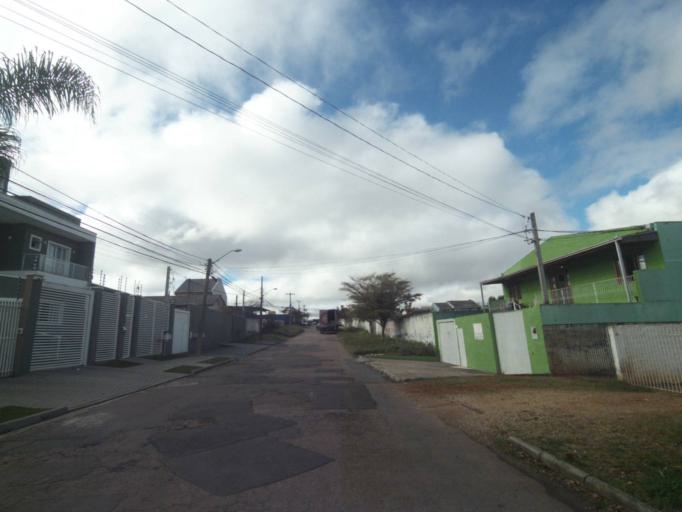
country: BR
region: Parana
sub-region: Sao Jose Dos Pinhais
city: Sao Jose dos Pinhais
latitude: -25.5244
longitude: -49.3000
